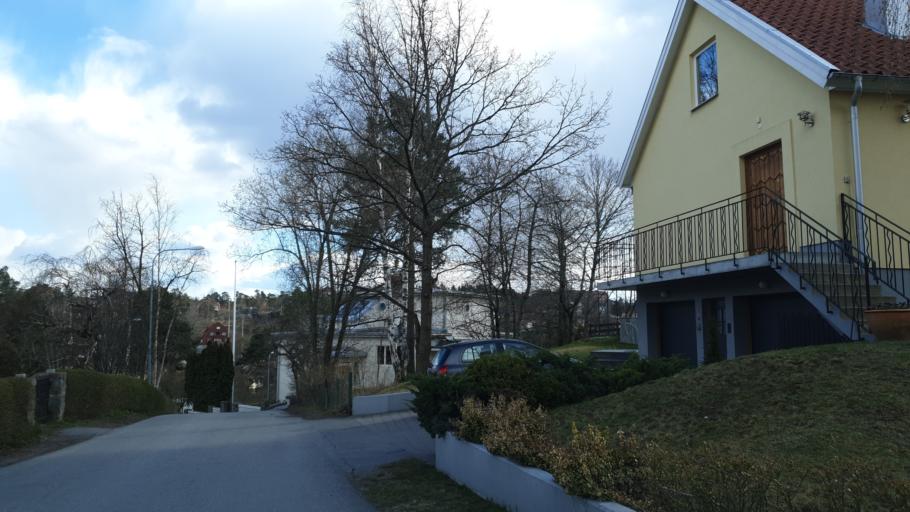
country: SE
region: Stockholm
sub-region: Lidingo
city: Lidingoe
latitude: 59.3715
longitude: 18.1228
